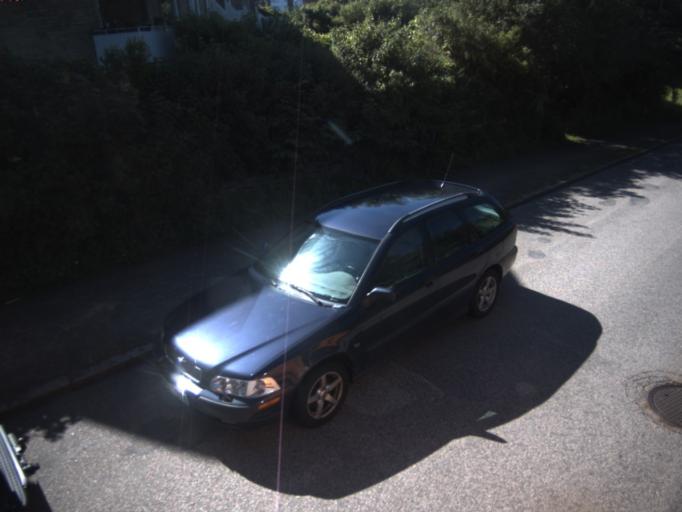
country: SE
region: Skane
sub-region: Helsingborg
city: Helsingborg
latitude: 56.0629
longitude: 12.6989
